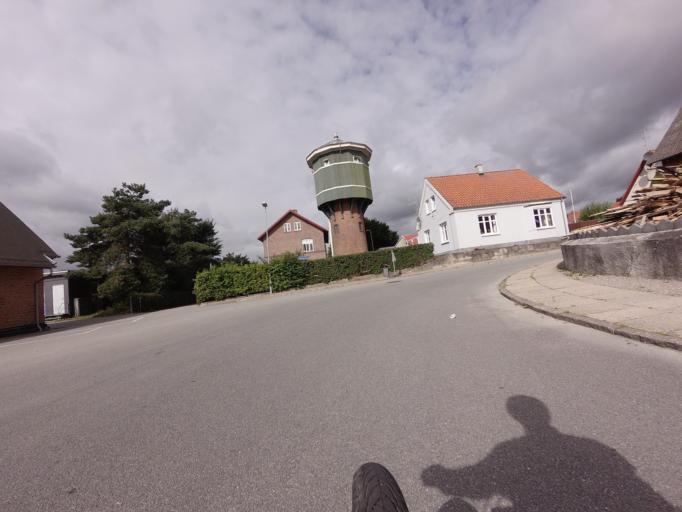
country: DK
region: Central Jutland
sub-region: Syddjurs Kommune
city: Ryomgard
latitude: 56.3804
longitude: 10.5000
